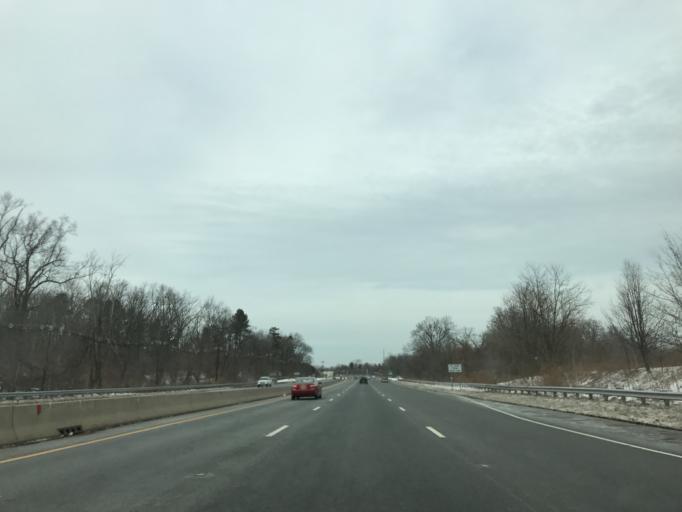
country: US
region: New Jersey
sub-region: Somerset County
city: Somerville
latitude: 40.5509
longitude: -74.6147
